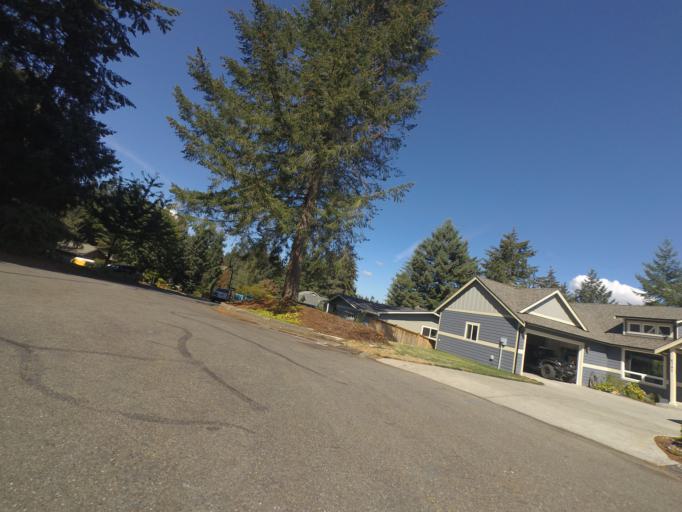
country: US
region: Washington
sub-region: Pierce County
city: Fircrest
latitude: 47.2142
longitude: -122.5170
